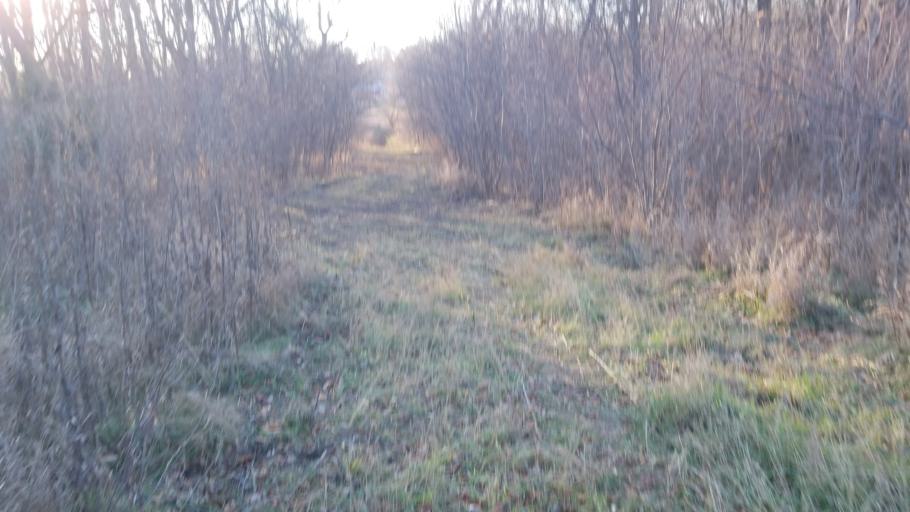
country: US
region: Nebraska
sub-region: Sarpy County
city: Offutt Air Force Base
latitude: 41.1661
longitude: -95.9602
